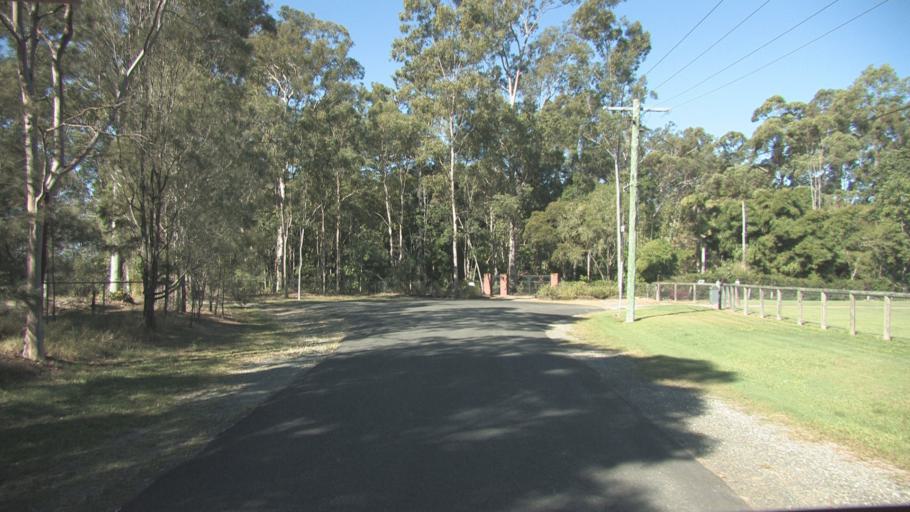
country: AU
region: Queensland
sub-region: Logan
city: Logan Reserve
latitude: -27.7380
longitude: 153.1240
